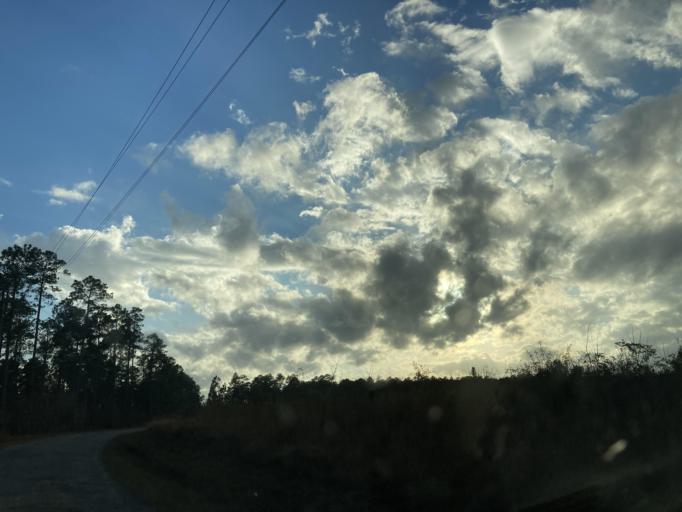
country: US
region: Mississippi
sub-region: Lamar County
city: Purvis
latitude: 31.1966
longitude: -89.5998
